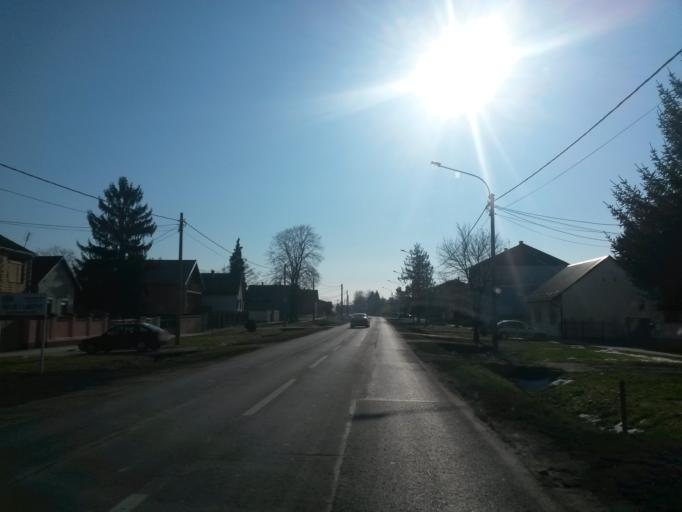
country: HR
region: Osjecko-Baranjska
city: Sarvas
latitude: 45.5227
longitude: 18.8442
